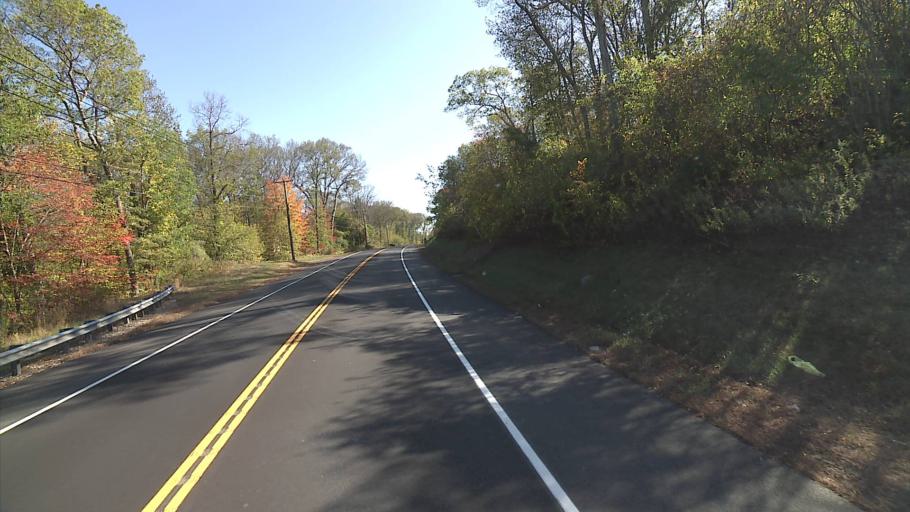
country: US
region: Connecticut
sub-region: Tolland County
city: Coventry Lake
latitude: 41.7317
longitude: -72.3334
